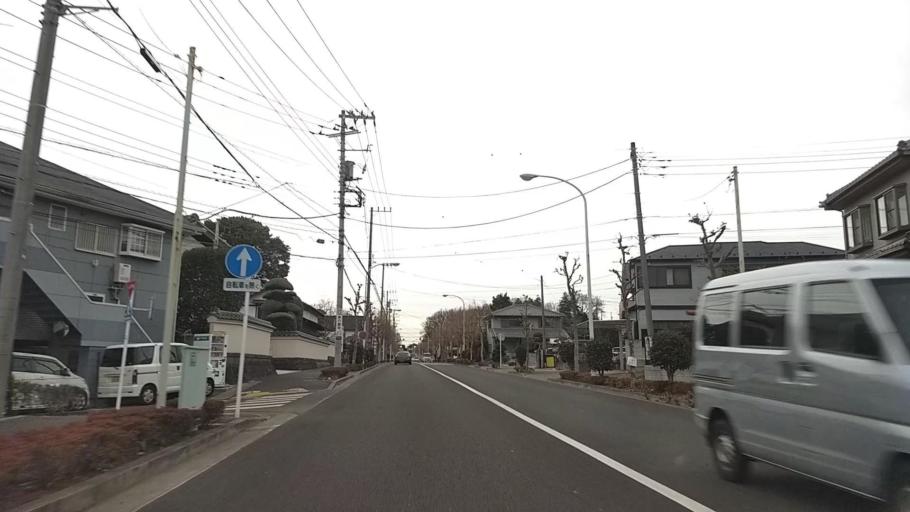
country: JP
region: Tokyo
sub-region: Machida-shi
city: Machida
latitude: 35.5203
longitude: 139.4633
